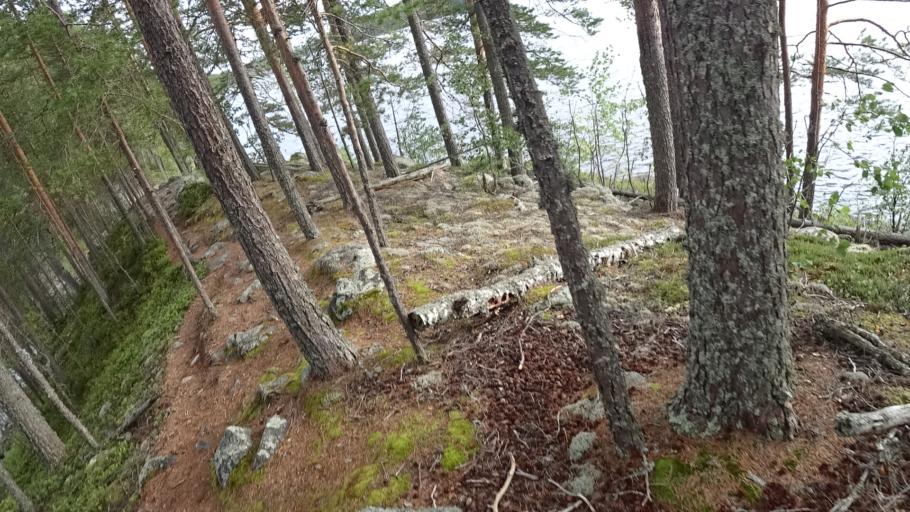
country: FI
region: North Karelia
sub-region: Joensuu
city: Ilomantsi
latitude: 62.5736
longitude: 31.1729
